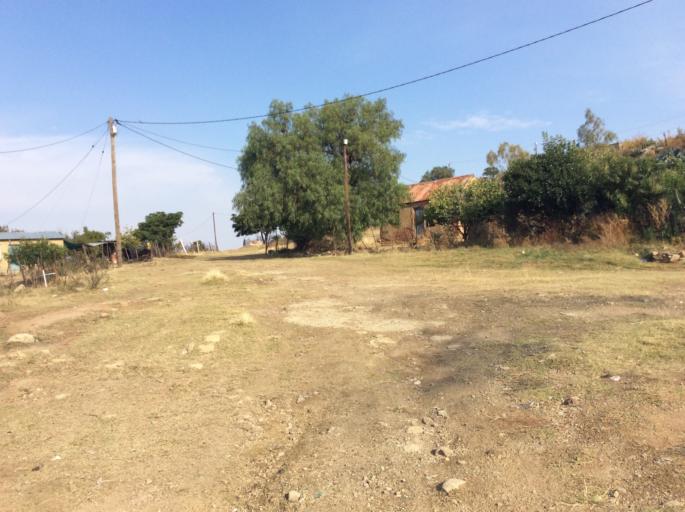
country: LS
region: Mafeteng
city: Mafeteng
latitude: -29.7239
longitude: 27.0341
